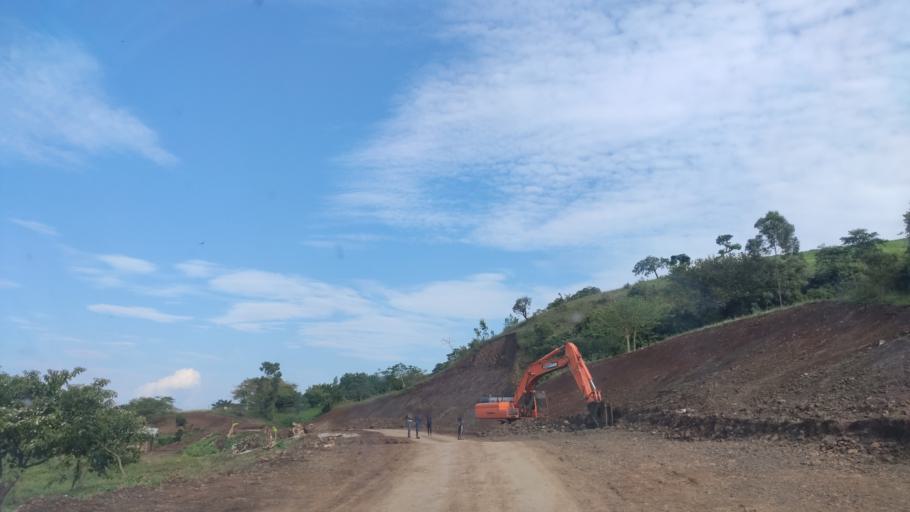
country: ET
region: Southern Nations, Nationalities, and People's Region
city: Arba Minch'
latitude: 6.4208
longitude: 37.3557
